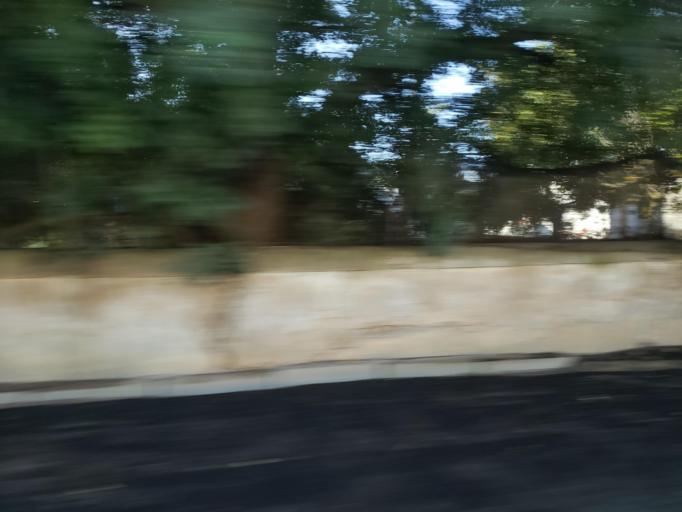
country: PT
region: Faro
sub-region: Portimao
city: Portimao
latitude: 37.1522
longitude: -8.5568
